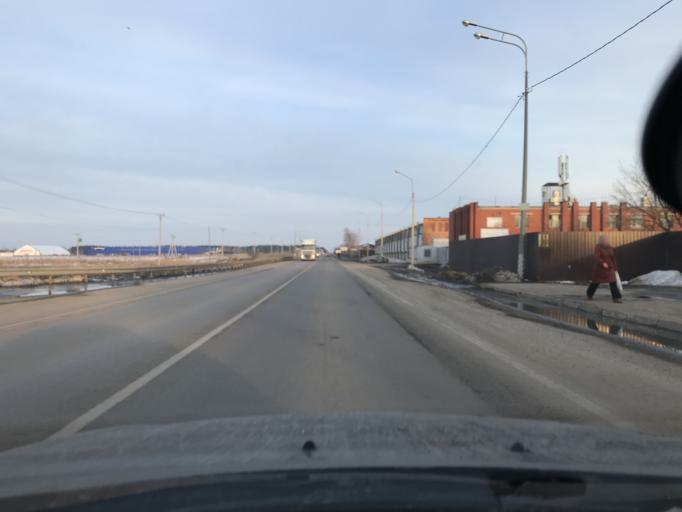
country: RU
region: Kaluga
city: Kaluga
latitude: 54.4679
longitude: 36.2431
